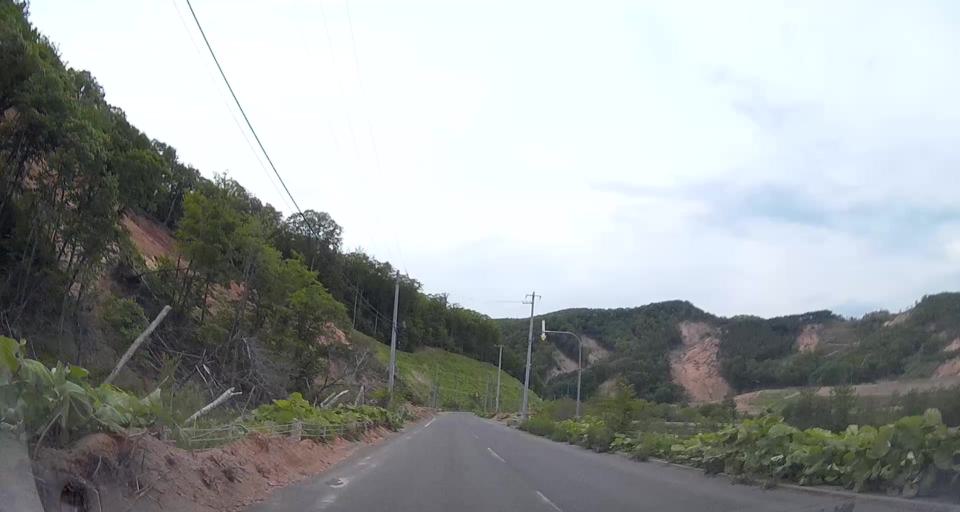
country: JP
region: Hokkaido
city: Chitose
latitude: 42.7635
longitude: 141.9886
